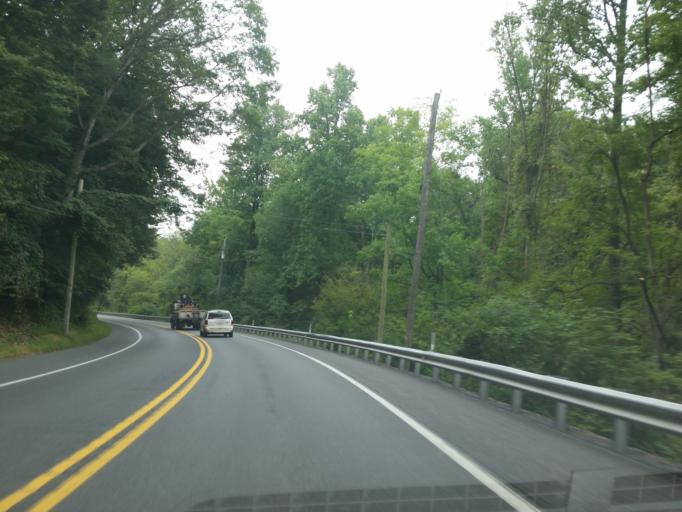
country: US
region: Pennsylvania
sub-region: Lancaster County
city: Brickerville
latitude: 40.2154
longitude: -76.3019
